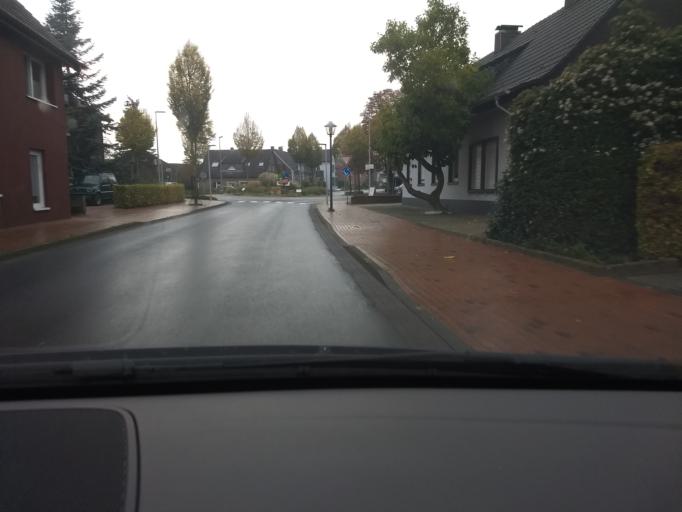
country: DE
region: North Rhine-Westphalia
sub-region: Regierungsbezirk Munster
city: Raesfeld
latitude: 51.7713
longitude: 6.8389
